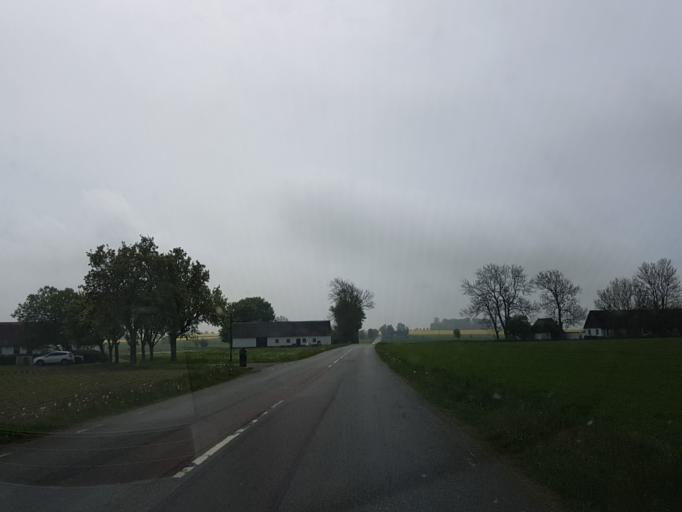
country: SE
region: Skane
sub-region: Tomelilla Kommun
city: Tomelilla
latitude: 55.4810
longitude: 14.1007
